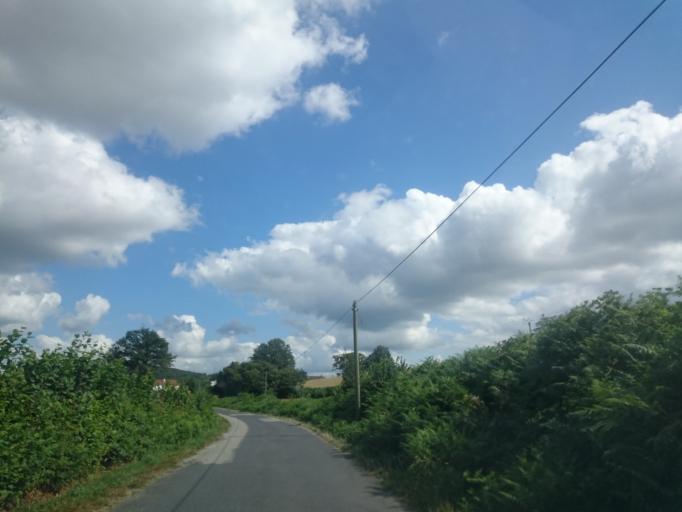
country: FR
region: Auvergne
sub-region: Departement du Cantal
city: Saint-Mamet-la-Salvetat
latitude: 44.8770
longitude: 2.2586
